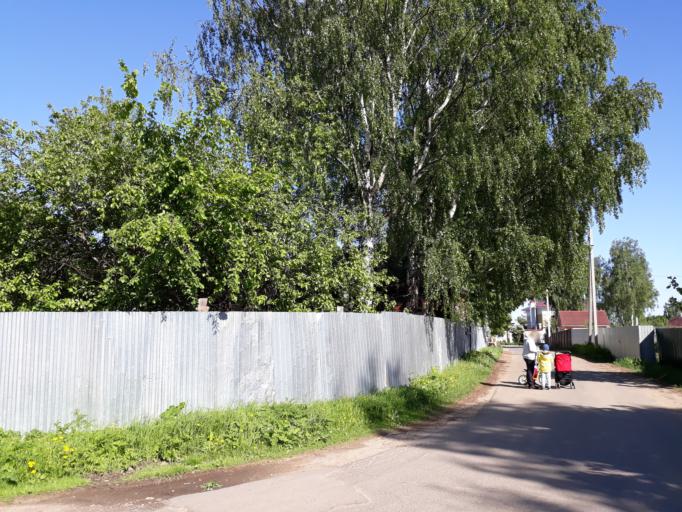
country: RU
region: Jaroslavl
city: Krasnyy Profintern
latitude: 57.8672
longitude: 40.2685
